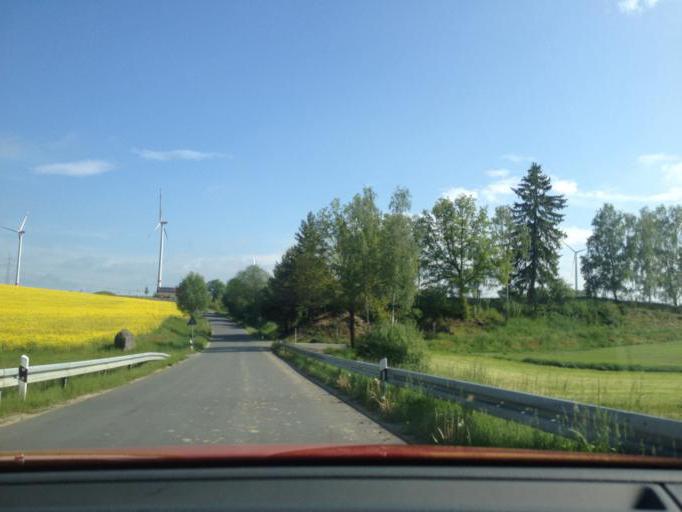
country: DE
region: Bavaria
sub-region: Upper Franconia
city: Thiersheim
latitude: 50.0312
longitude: 12.1296
